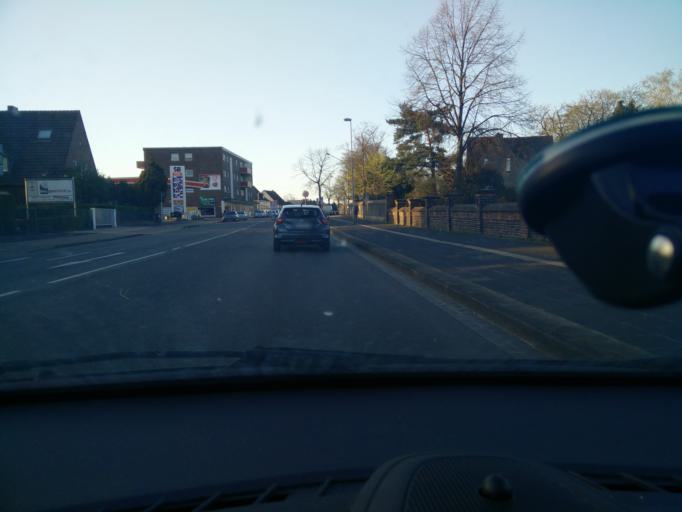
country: DE
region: North Rhine-Westphalia
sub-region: Regierungsbezirk Dusseldorf
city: Moers
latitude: 51.4525
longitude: 6.6382
